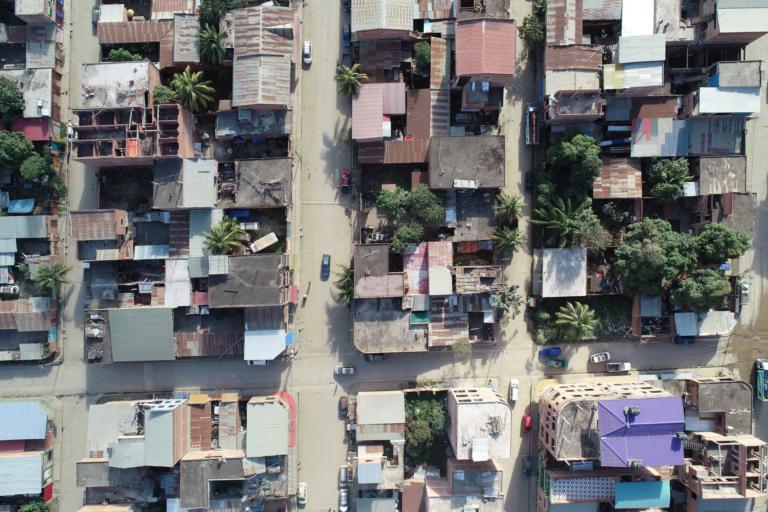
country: BO
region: La Paz
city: Coroico
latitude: -15.8360
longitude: -67.5614
